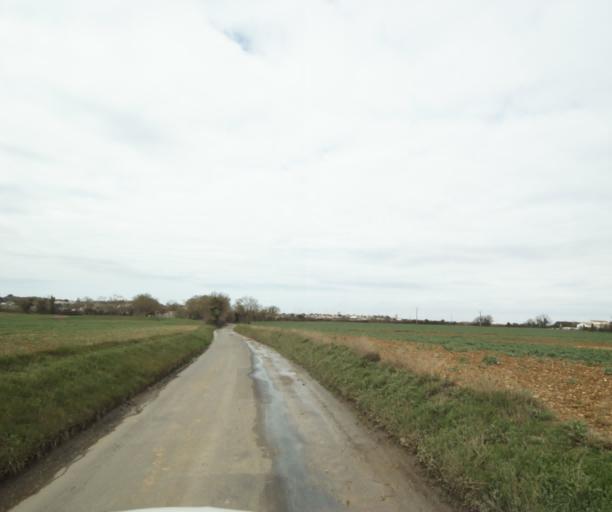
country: FR
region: Poitou-Charentes
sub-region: Departement de la Charente-Maritime
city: Nieul-sur-Mer
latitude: 46.1904
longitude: -1.1725
